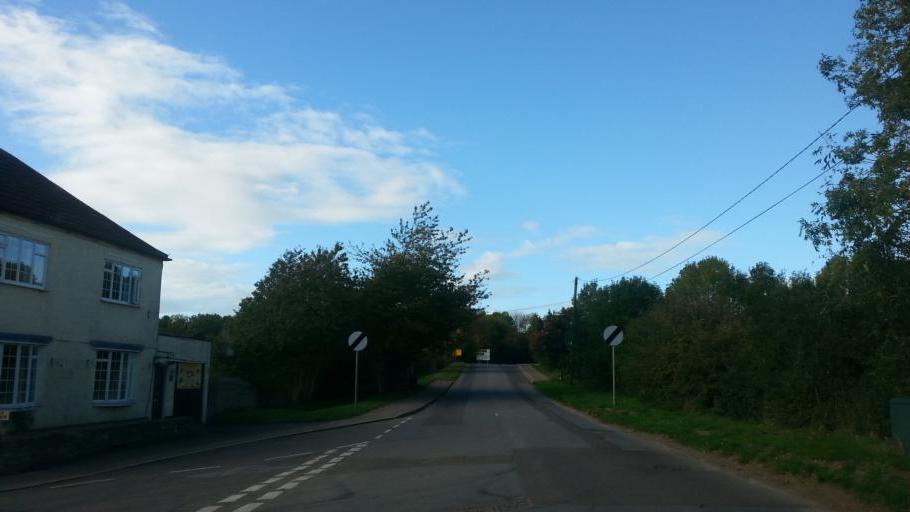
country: GB
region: England
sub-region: District of Rutland
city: Greetham
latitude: 52.8112
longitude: -0.6218
